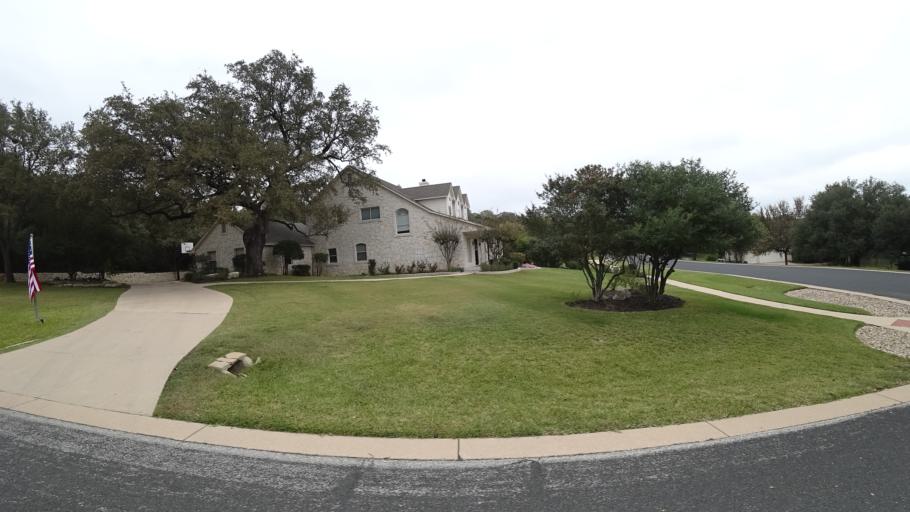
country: US
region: Texas
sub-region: Williamson County
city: Anderson Mill
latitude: 30.4465
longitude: -97.8224
